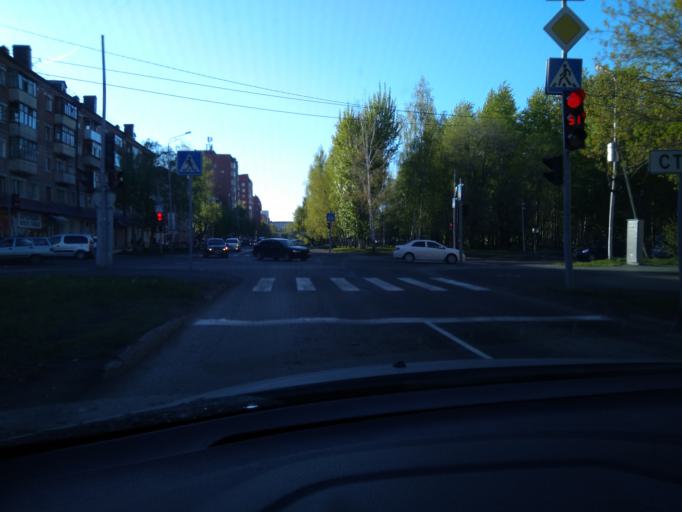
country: RU
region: Tjumen
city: Tyumen
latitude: 57.1325
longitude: 65.5855
